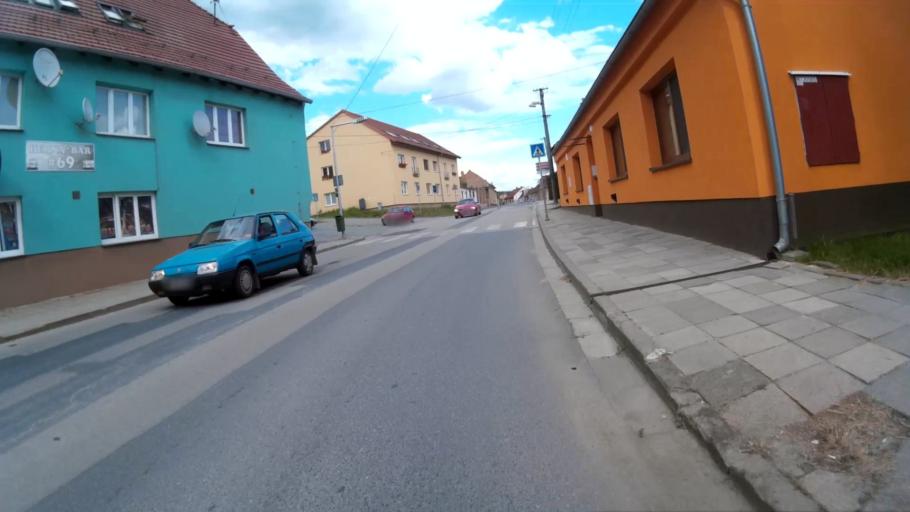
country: CZ
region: South Moravian
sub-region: Okres Brno-Venkov
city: Rosice
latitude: 49.1799
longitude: 16.3875
